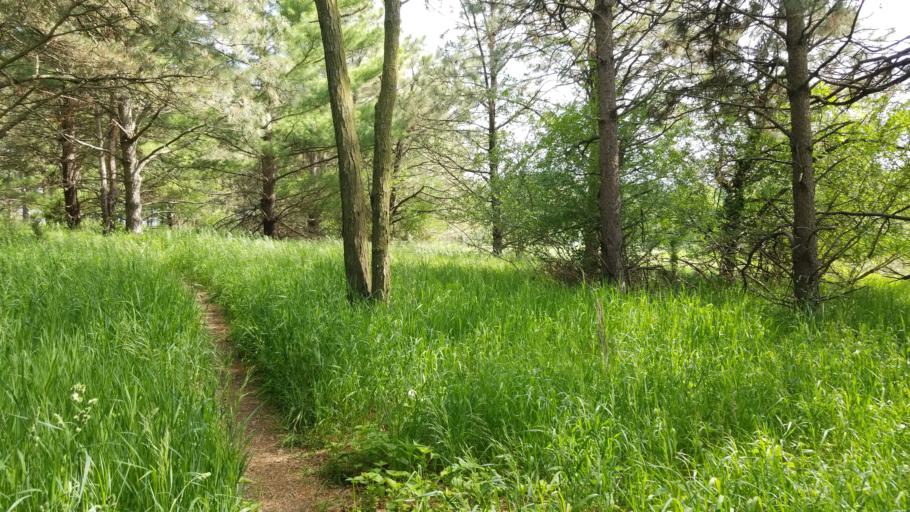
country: US
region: Nebraska
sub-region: Sarpy County
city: Chalco
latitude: 41.1729
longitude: -96.1599
